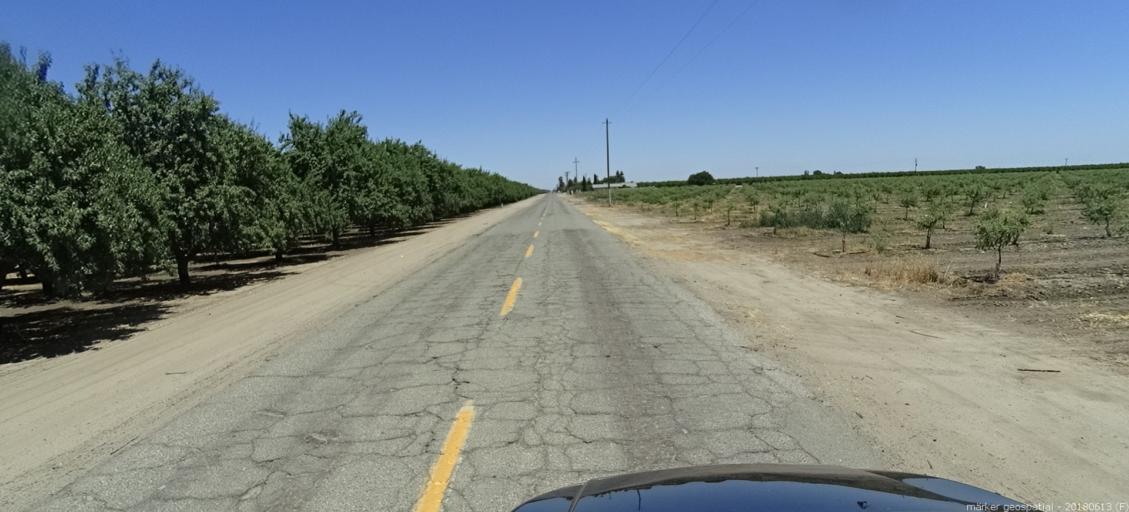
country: US
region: California
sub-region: Madera County
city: Fairmead
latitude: 36.9964
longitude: -120.2509
